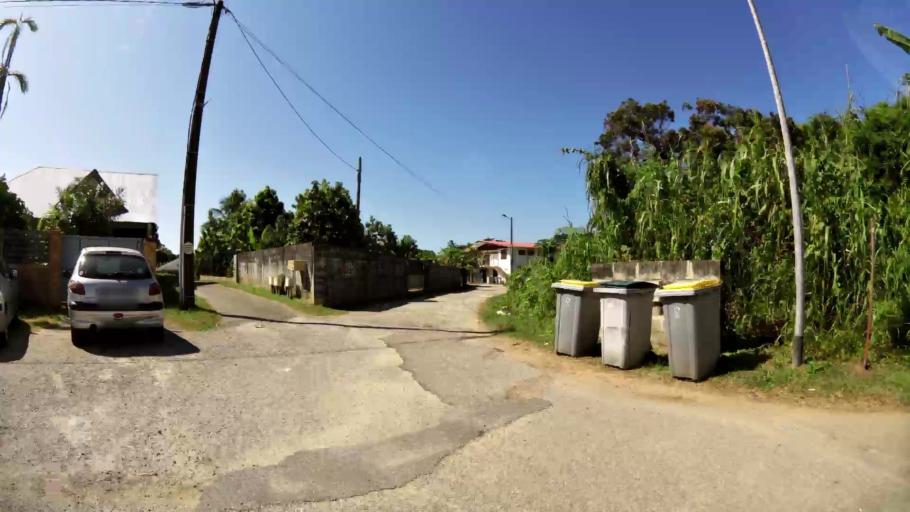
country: GF
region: Guyane
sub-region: Guyane
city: Remire-Montjoly
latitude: 4.9169
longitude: -52.2707
